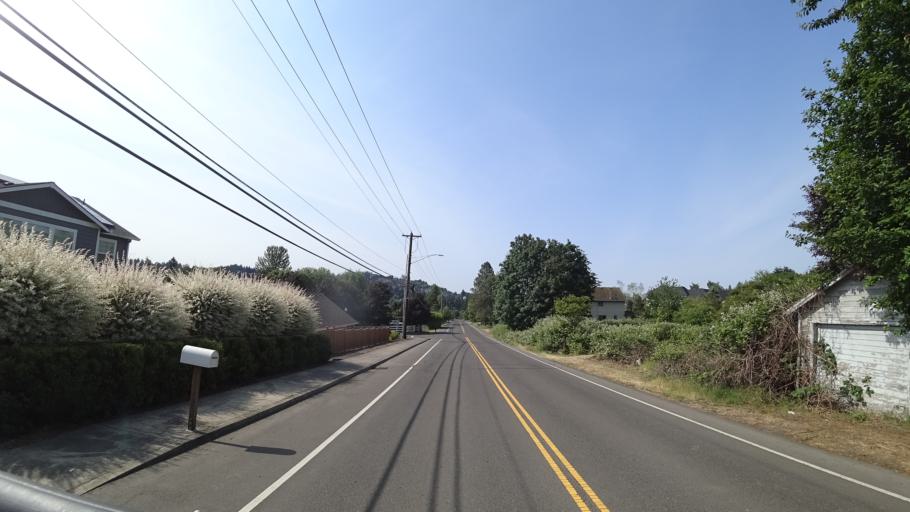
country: US
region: Oregon
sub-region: Clackamas County
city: Happy Valley
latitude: 45.4512
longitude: -122.5275
